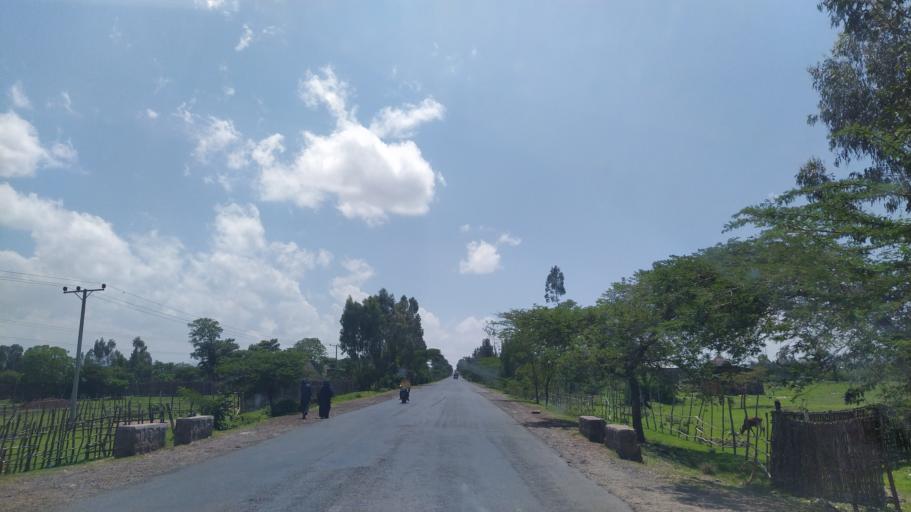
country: ET
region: Southern Nations, Nationalities, and People's Region
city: K'olito
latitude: 7.7489
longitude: 38.1270
